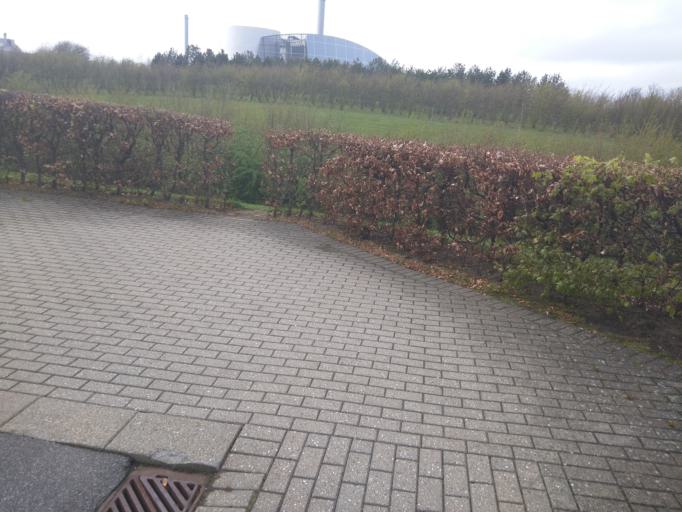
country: DK
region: Central Jutland
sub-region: Viborg Kommune
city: Viborg
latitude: 56.4717
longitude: 9.4181
